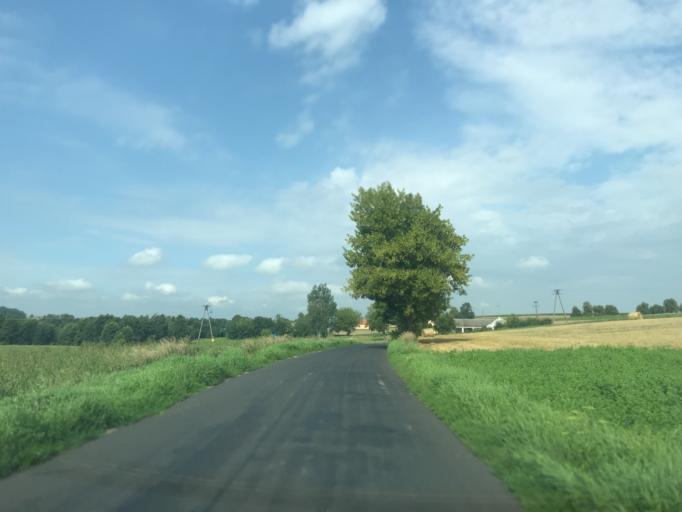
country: PL
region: Warmian-Masurian Voivodeship
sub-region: Powiat nowomiejski
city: Kurzetnik
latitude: 53.3685
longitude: 19.5812
